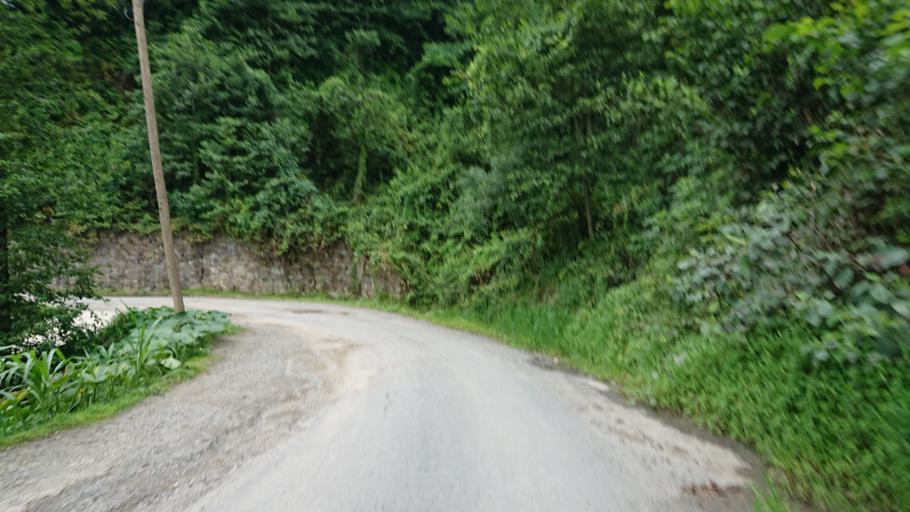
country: TR
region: Rize
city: Rize
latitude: 40.9669
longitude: 40.5112
